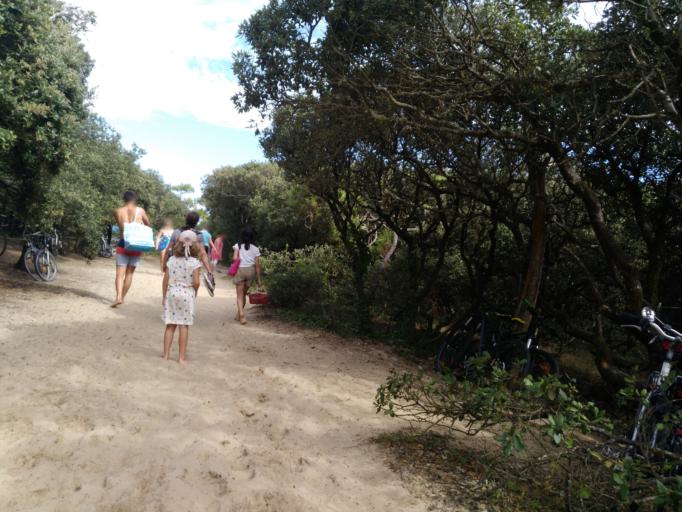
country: FR
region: Poitou-Charentes
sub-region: Departement de la Charente-Maritime
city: Les Mathes
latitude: 45.6975
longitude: -1.2334
